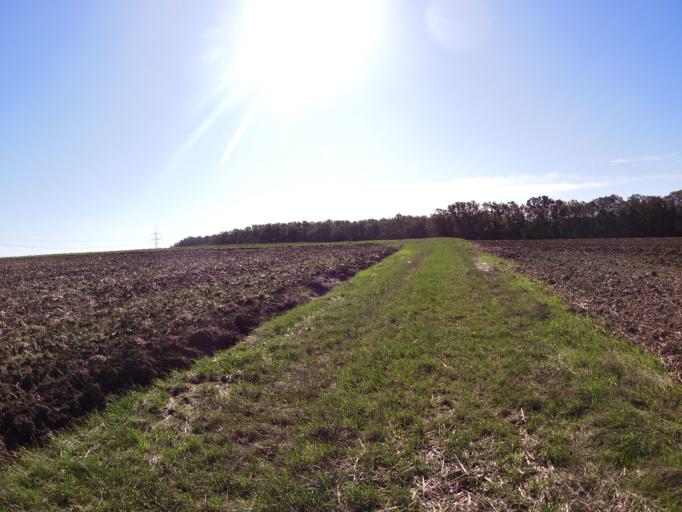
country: DE
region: Bavaria
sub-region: Regierungsbezirk Unterfranken
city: Theilheim
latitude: 49.7483
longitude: 10.0433
